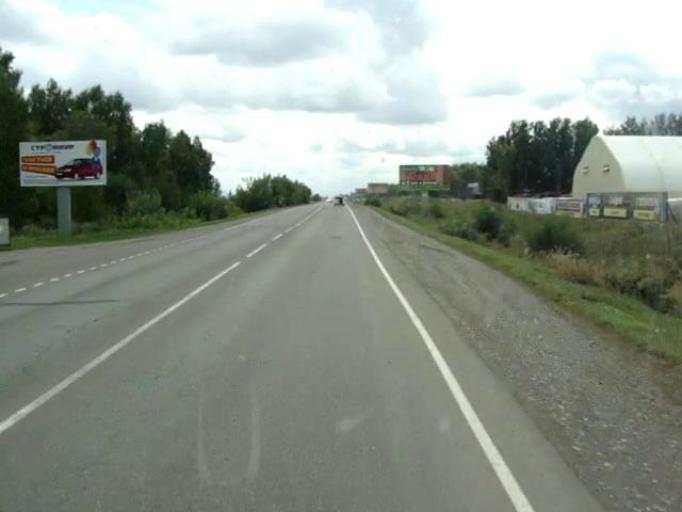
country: RU
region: Altai Krai
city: Zarya
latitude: 52.5746
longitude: 85.1809
